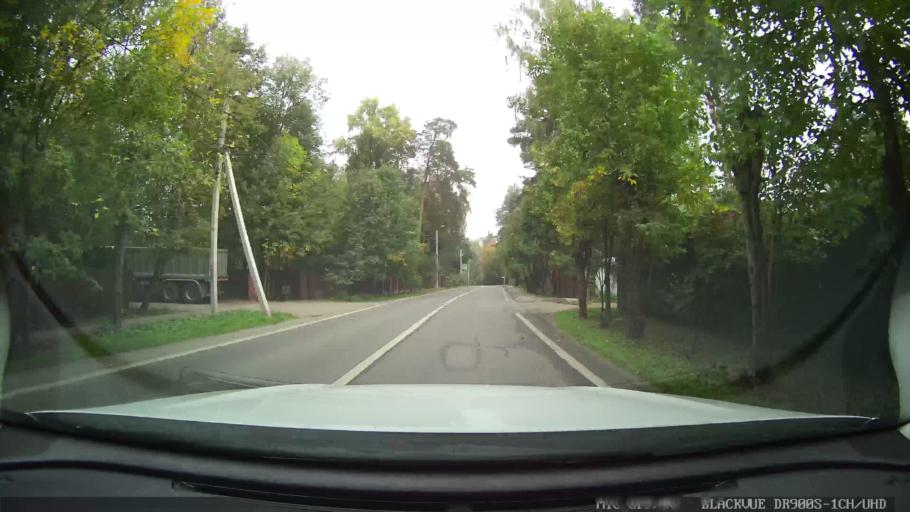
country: RU
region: Moscow
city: Novo-Peredelkino
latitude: 55.6516
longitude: 37.3555
